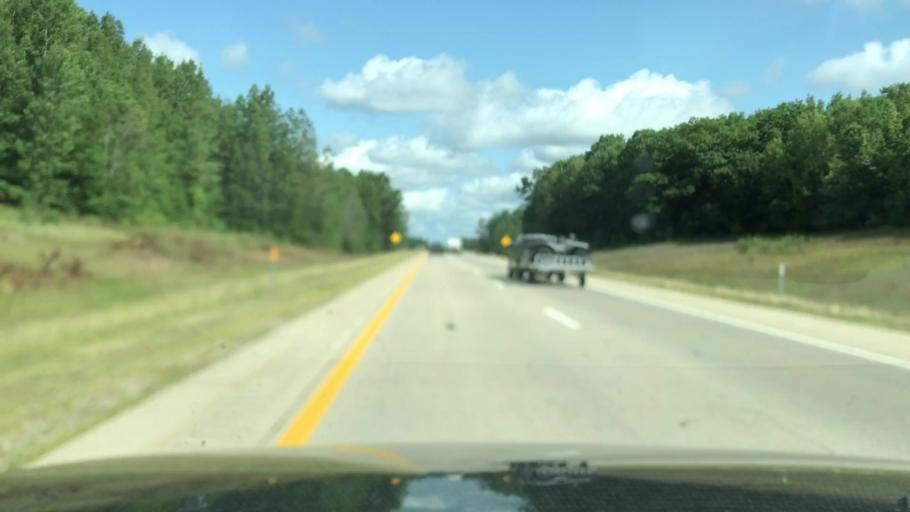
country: US
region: Michigan
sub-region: Montcalm County
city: Howard City
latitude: 43.3631
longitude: -85.5132
